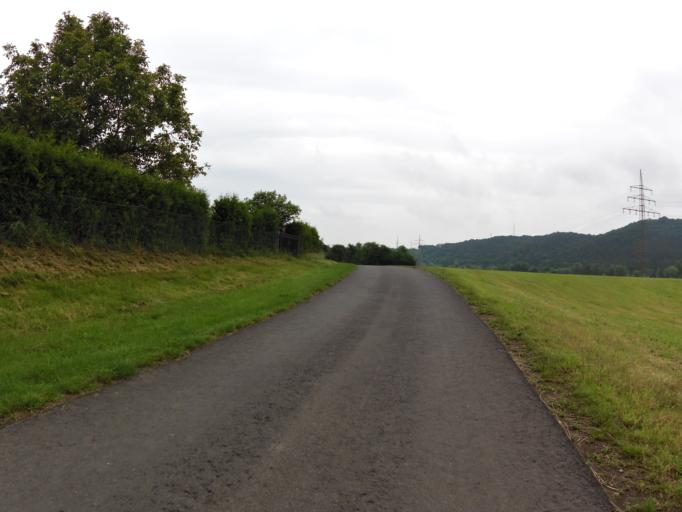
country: DE
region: Hesse
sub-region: Regierungsbezirk Kassel
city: Bad Hersfeld
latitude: 50.8996
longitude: 9.7481
